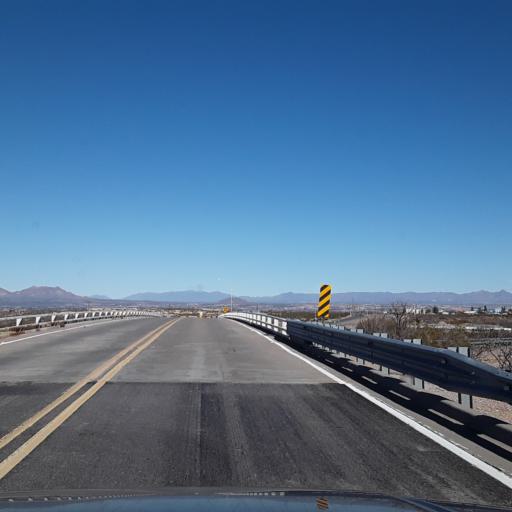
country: US
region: New Mexico
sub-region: Dona Ana County
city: Mesilla
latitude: 32.2814
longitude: -106.8831
